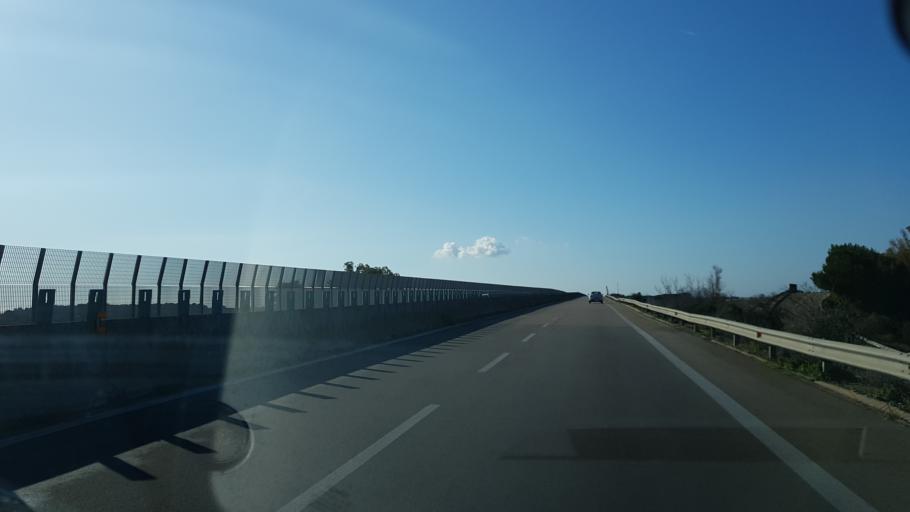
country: IT
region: Apulia
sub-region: Provincia di Lecce
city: Sannicola
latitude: 40.1157
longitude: 18.0437
